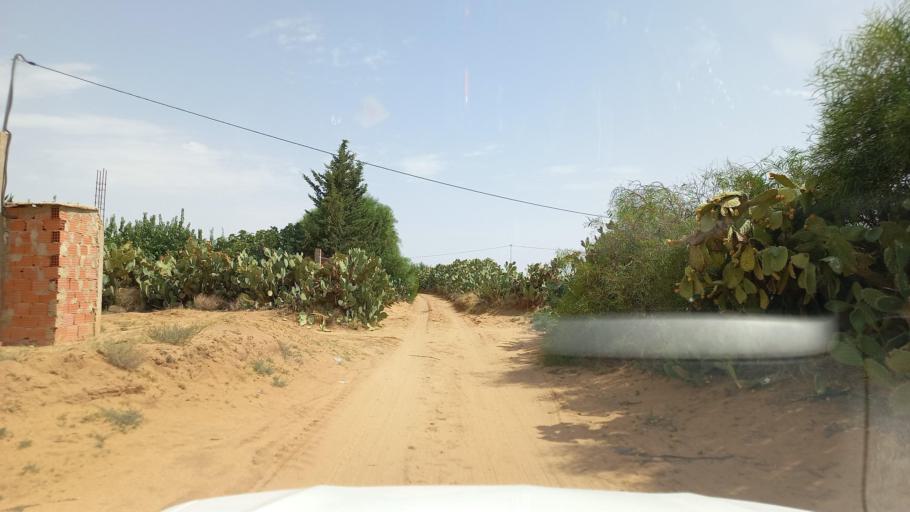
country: TN
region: Al Qasrayn
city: Kasserine
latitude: 35.2494
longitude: 9.0615
